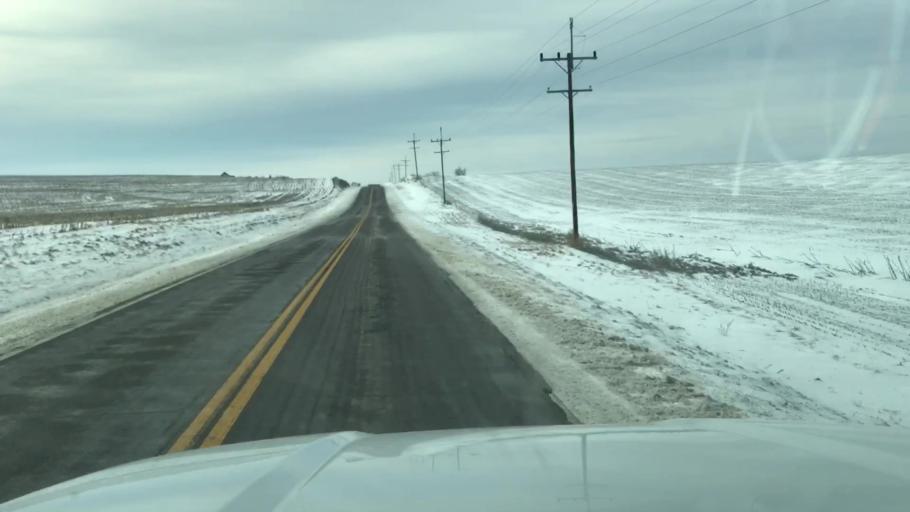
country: US
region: Missouri
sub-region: Holt County
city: Mound City
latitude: 40.1081
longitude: -95.1450
